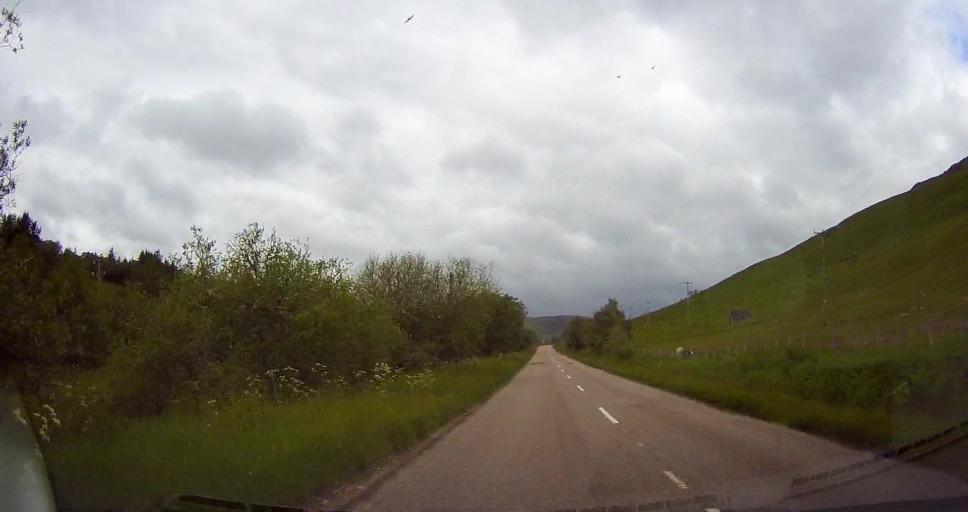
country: GB
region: Scotland
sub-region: Highland
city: Dornoch
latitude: 58.0050
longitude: -4.2254
